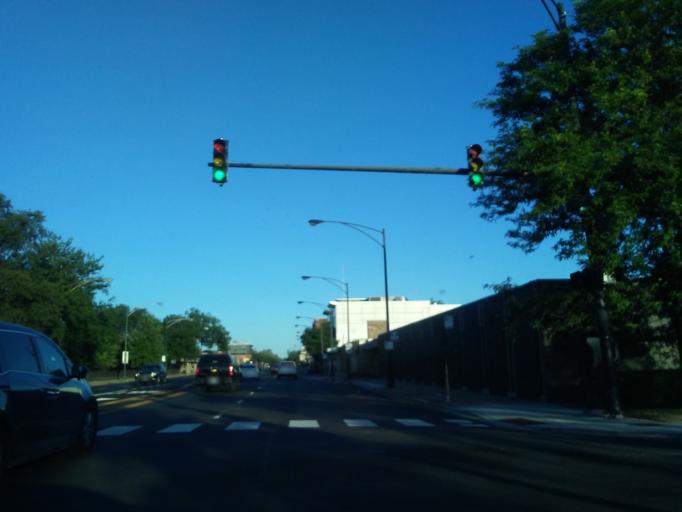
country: US
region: Illinois
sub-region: Cook County
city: Lincolnwood
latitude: 41.9905
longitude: -87.7111
